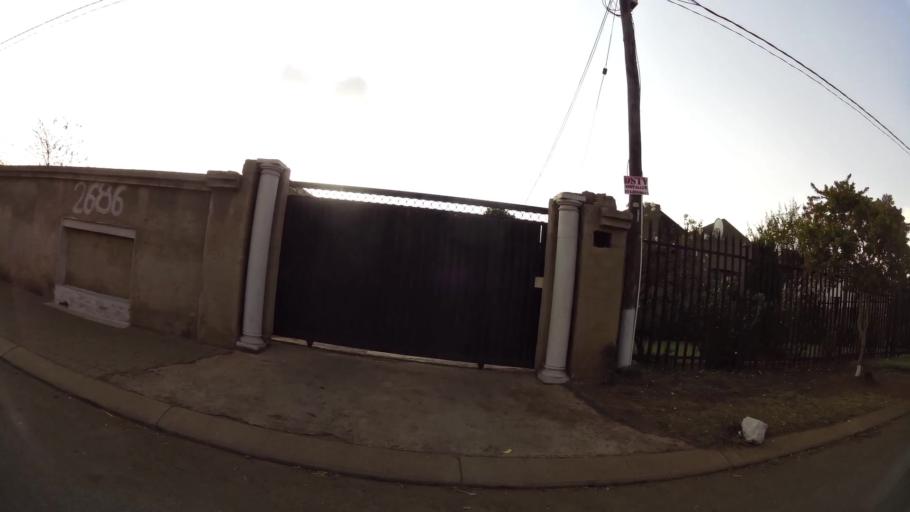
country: ZA
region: Gauteng
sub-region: Ekurhuleni Metropolitan Municipality
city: Tembisa
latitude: -25.9509
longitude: 28.2121
